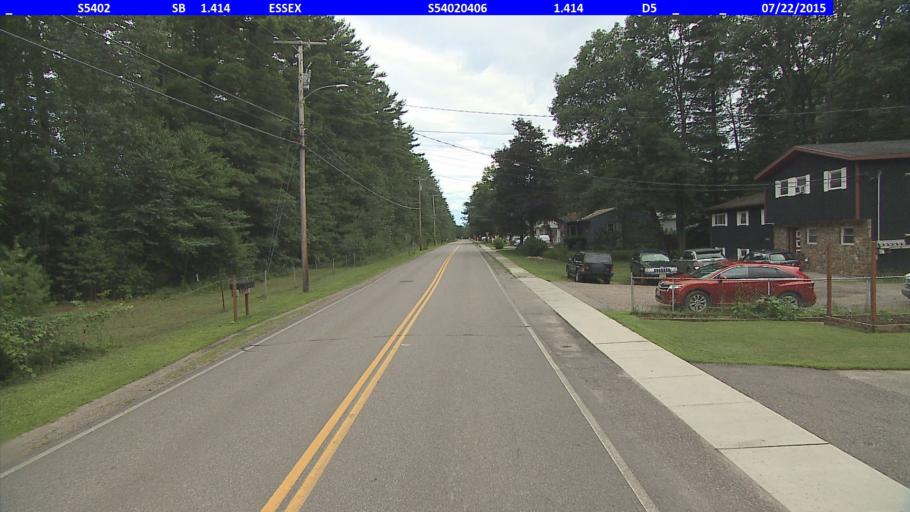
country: US
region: Vermont
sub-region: Chittenden County
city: Jericho
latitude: 44.4986
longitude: -73.0493
